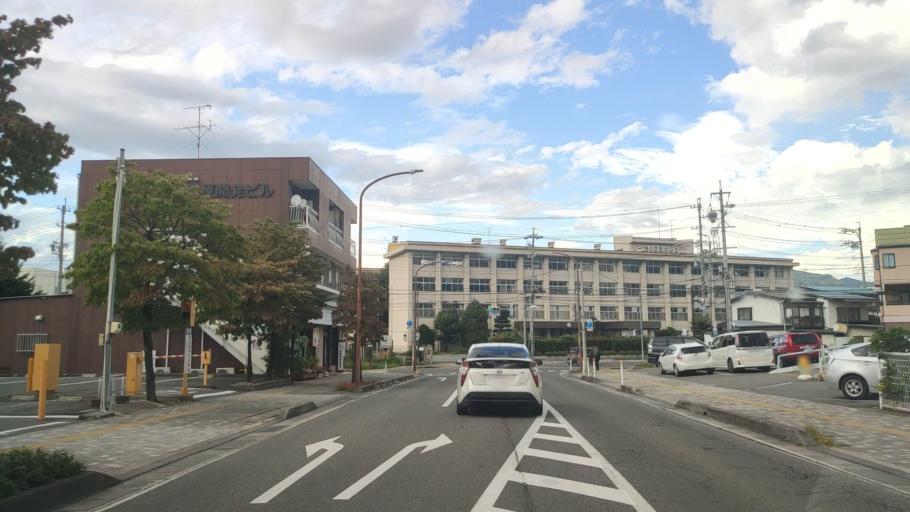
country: JP
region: Nagano
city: Suzaka
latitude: 36.6576
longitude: 138.3080
